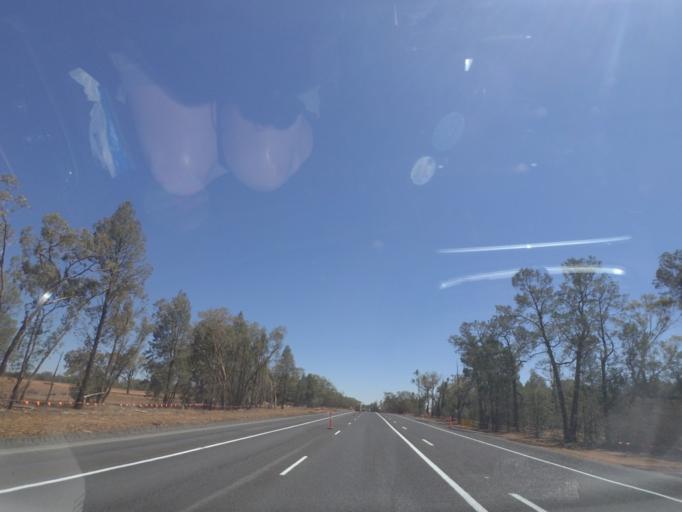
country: AU
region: New South Wales
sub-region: Gilgandra
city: Gilgandra
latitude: -31.6610
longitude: 148.7225
